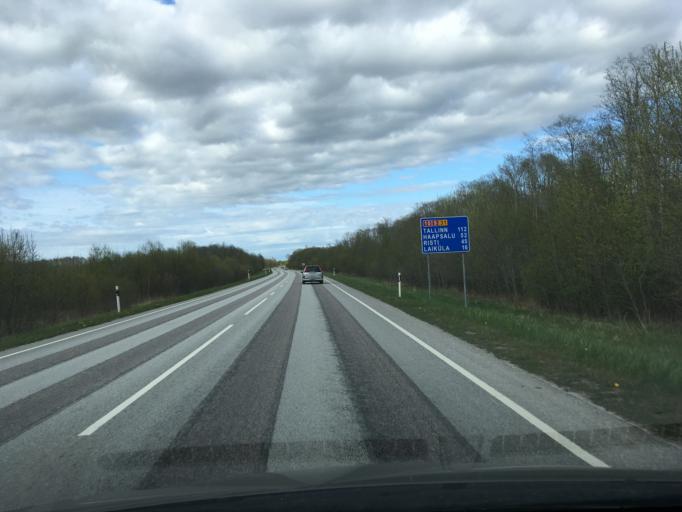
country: EE
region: Laeaene
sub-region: Lihula vald
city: Lihula
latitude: 58.6881
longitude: 23.8133
